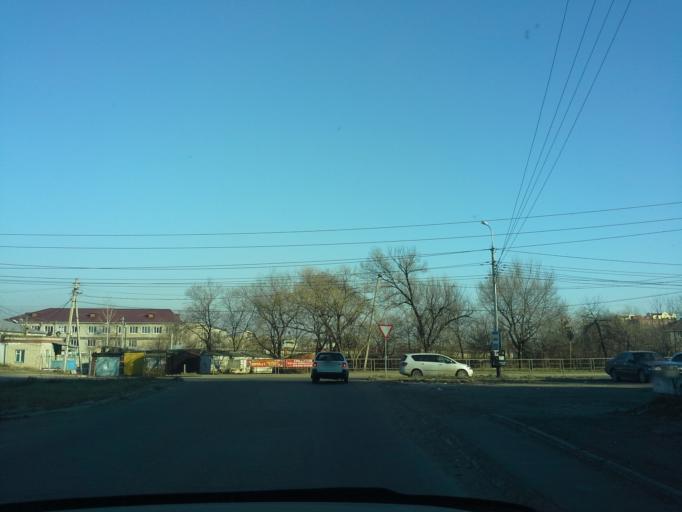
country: RU
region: Khabarovsk Krai
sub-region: Khabarovskiy Rayon
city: Khabarovsk
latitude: 48.4806
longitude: 135.1224
